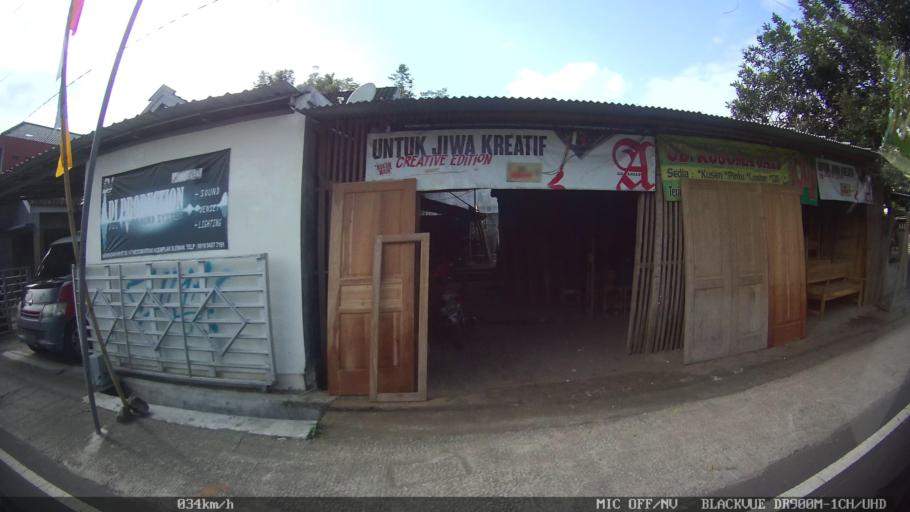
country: ID
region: Daerah Istimewa Yogyakarta
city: Depok
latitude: -7.7289
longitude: 110.4208
